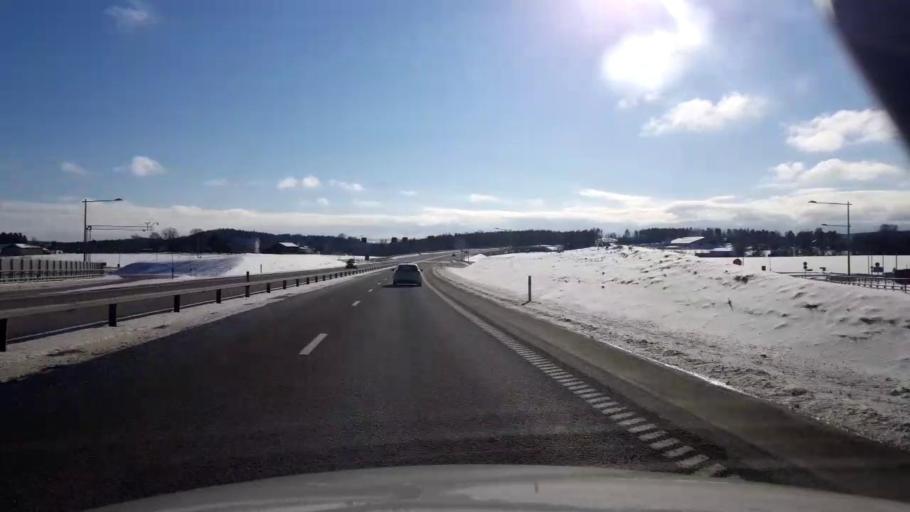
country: SE
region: Vaesternorrland
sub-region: Sundsvalls Kommun
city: Nolby
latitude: 62.2957
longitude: 17.3494
